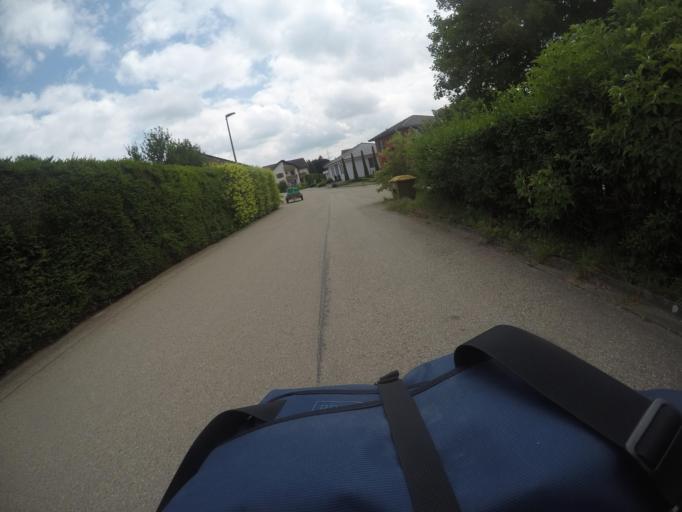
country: DE
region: Bavaria
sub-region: Swabia
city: Heimertingen
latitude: 48.0373
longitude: 10.1591
